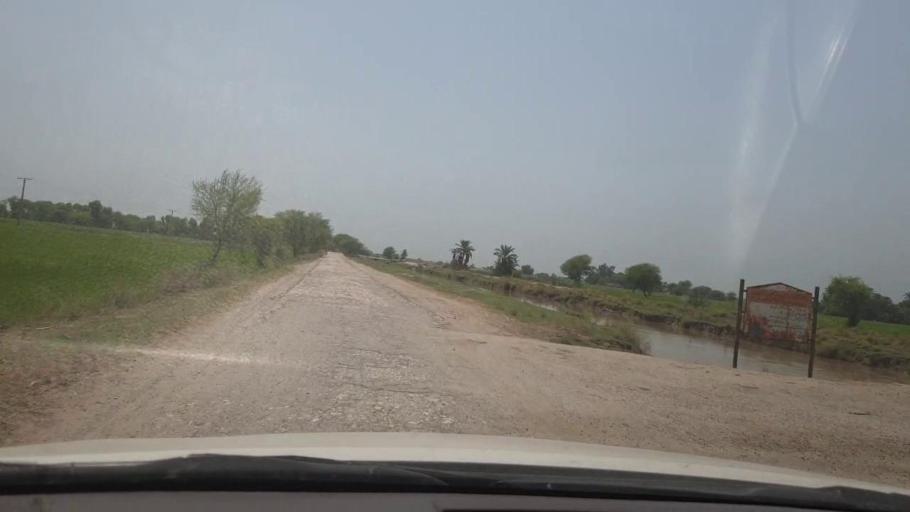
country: PK
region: Sindh
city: Shikarpur
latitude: 28.0962
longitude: 68.5785
